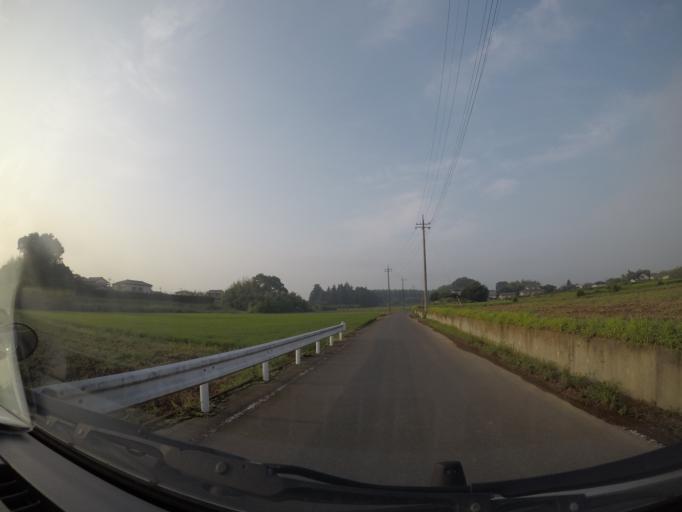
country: JP
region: Tochigi
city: Fujioka
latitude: 36.2665
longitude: 139.6770
